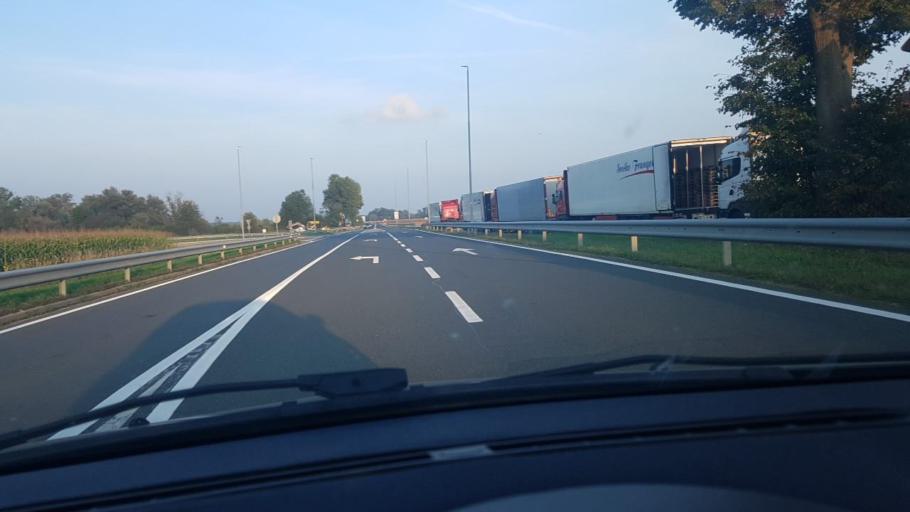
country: SI
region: Slovenska Bistrica
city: Pragersko
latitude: 46.4085
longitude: 15.7100
